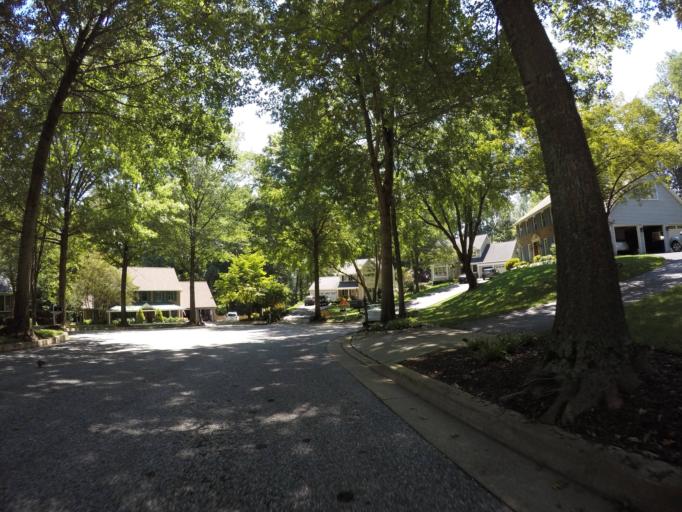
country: US
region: Maryland
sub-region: Howard County
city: Columbia
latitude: 39.2886
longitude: -76.8819
